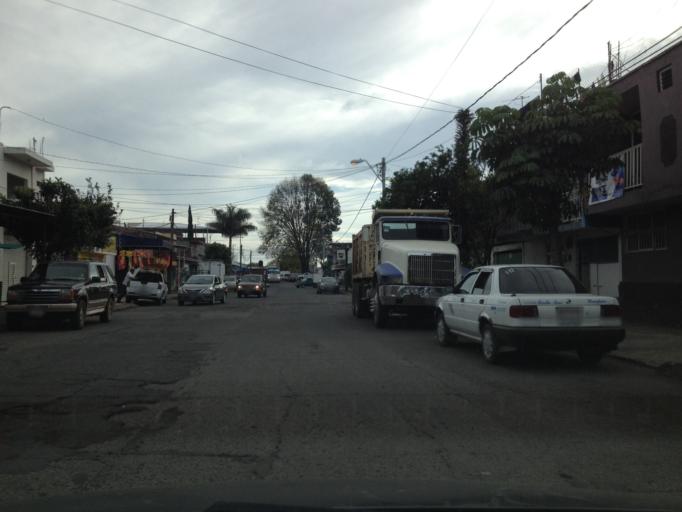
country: MX
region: Michoacan
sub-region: Uruapan
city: Uruapan
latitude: 19.4177
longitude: -102.0370
